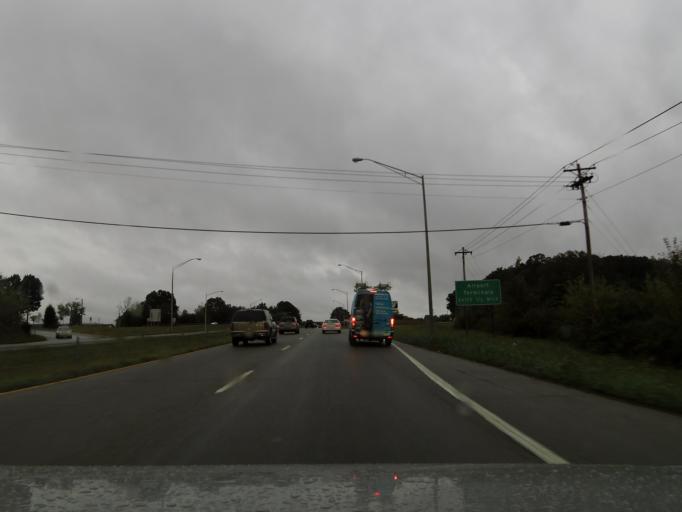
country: US
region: Tennessee
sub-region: Blount County
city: Alcoa
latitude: 35.7971
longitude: -83.9910
